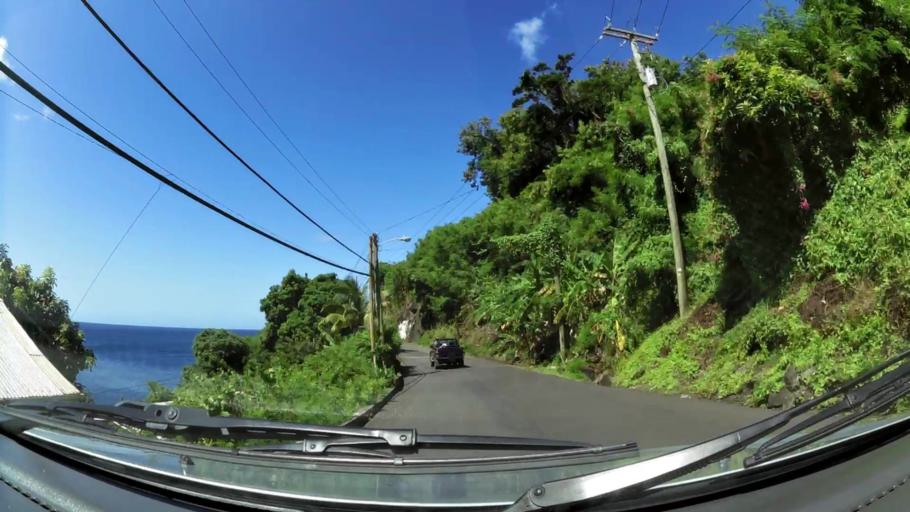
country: GD
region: Saint John
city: Gouyave
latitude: 12.1287
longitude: -61.7481
